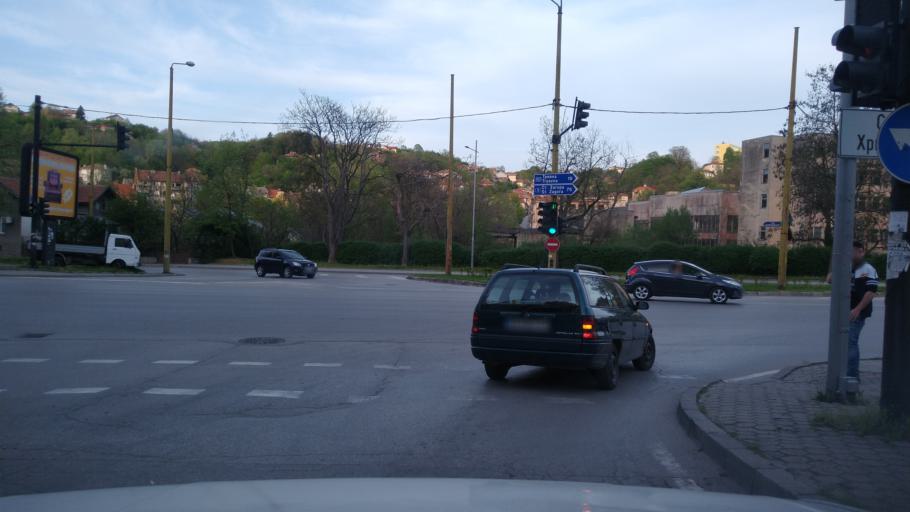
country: BG
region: Gabrovo
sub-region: Obshtina Gabrovo
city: Gabrovo
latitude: 42.8659
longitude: 25.3177
